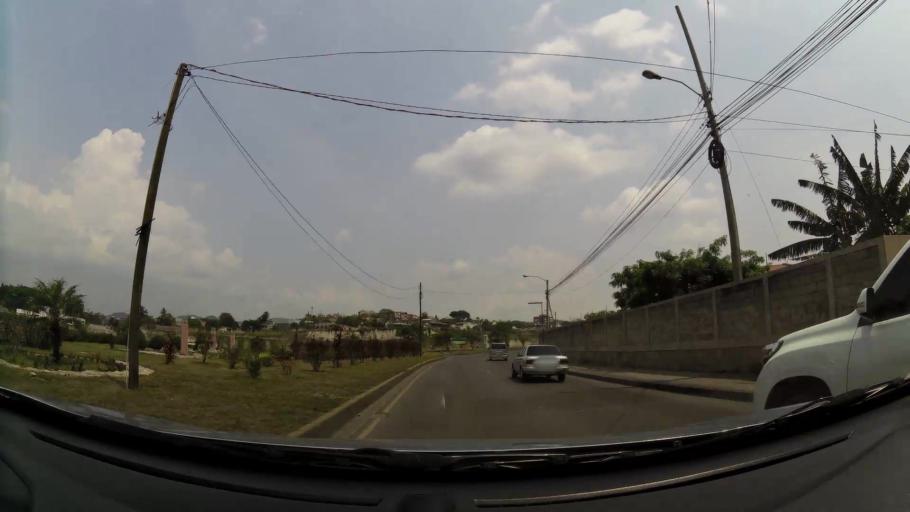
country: HN
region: Francisco Morazan
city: Tegucigalpa
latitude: 14.0532
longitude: -87.2215
